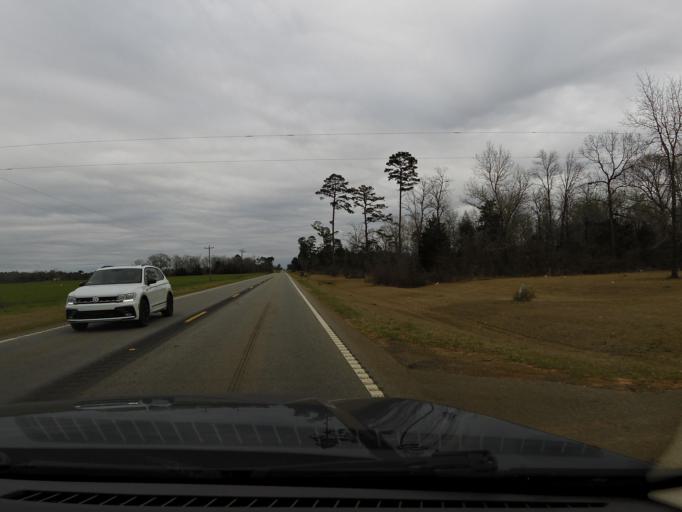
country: US
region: Georgia
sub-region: Randolph County
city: Shellman
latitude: 31.7726
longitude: -84.6601
